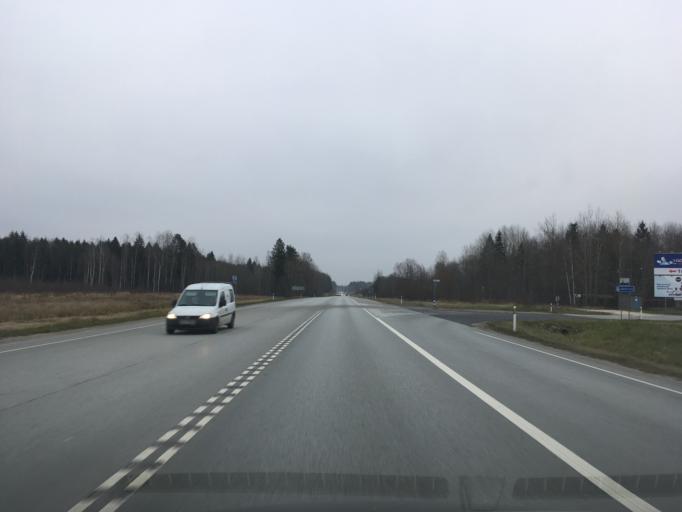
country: EE
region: Ida-Virumaa
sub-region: Johvi vald
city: Johvi
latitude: 59.3663
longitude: 27.4337
